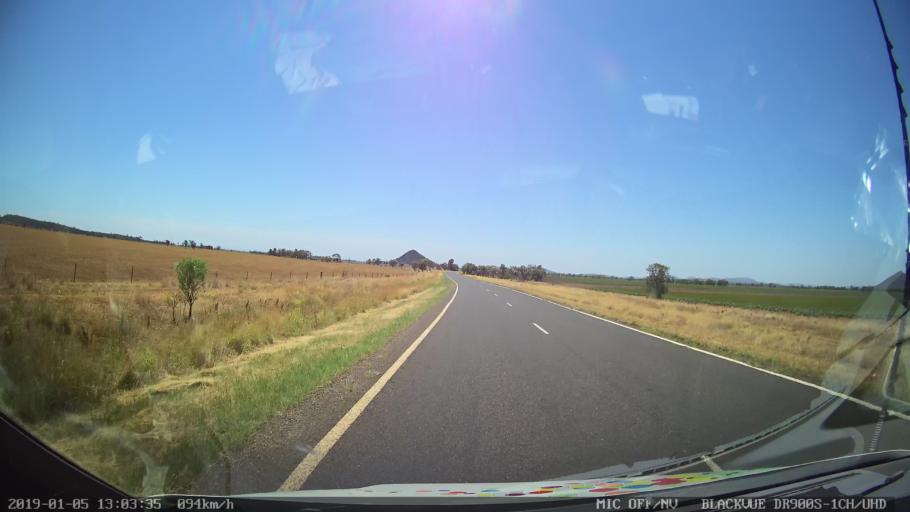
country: AU
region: New South Wales
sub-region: Gunnedah
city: Gunnedah
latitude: -31.1100
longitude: 149.8292
